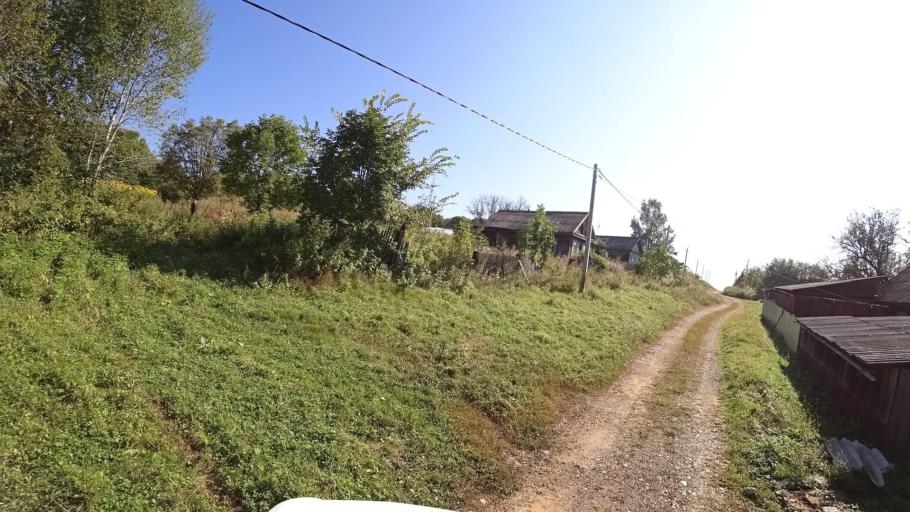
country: RU
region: Jewish Autonomous Oblast
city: Bira
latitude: 49.0071
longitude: 132.4666
